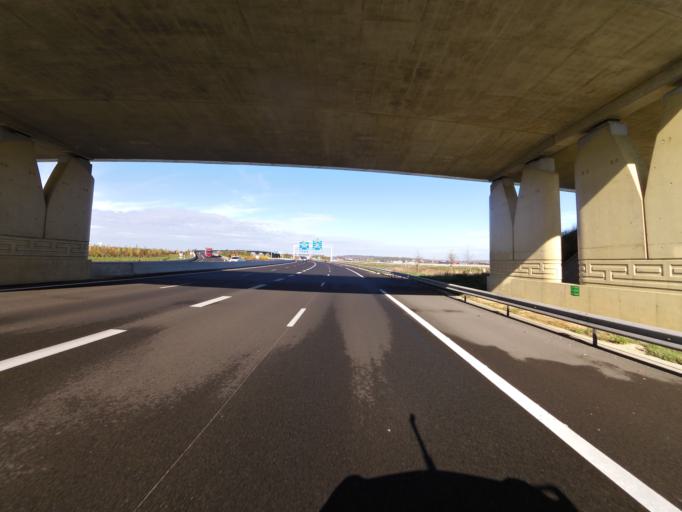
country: FR
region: Champagne-Ardenne
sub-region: Departement de la Marne
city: Tinqueux
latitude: 49.2402
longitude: 3.9682
